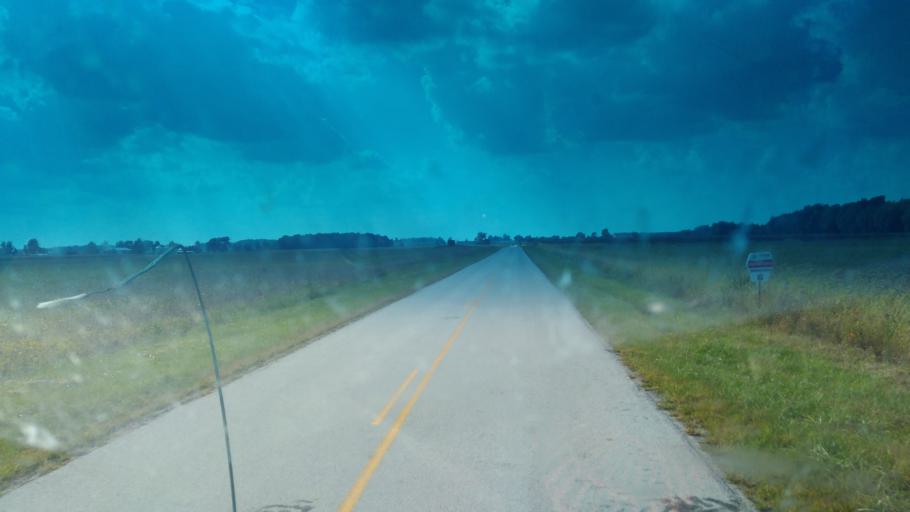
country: US
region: Ohio
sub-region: Hardin County
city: Kenton
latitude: 40.7461
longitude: -83.6214
